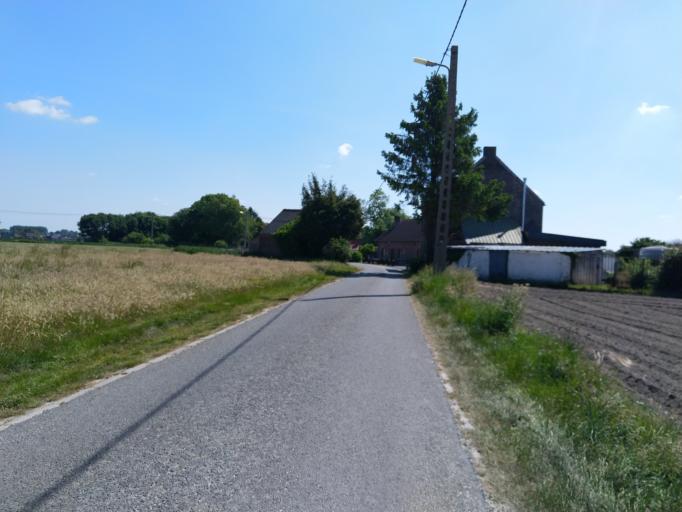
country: BE
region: Wallonia
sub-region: Province du Hainaut
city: Jurbise
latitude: 50.5138
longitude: 3.8584
